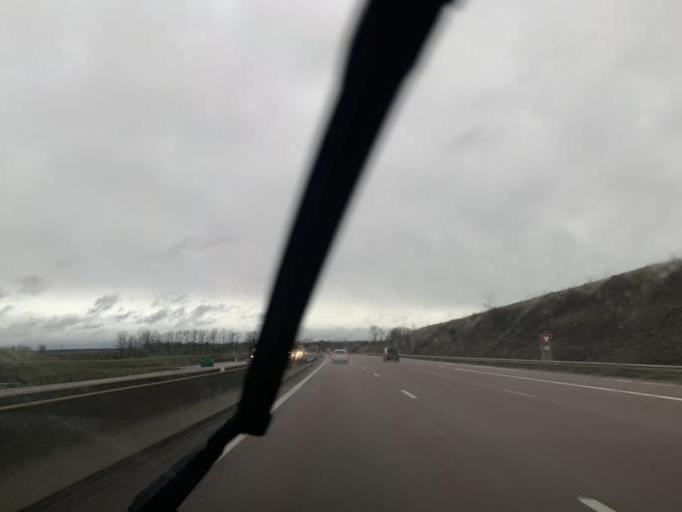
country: FR
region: Champagne-Ardenne
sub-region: Departement de la Haute-Marne
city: Langres
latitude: 47.7919
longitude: 5.2235
